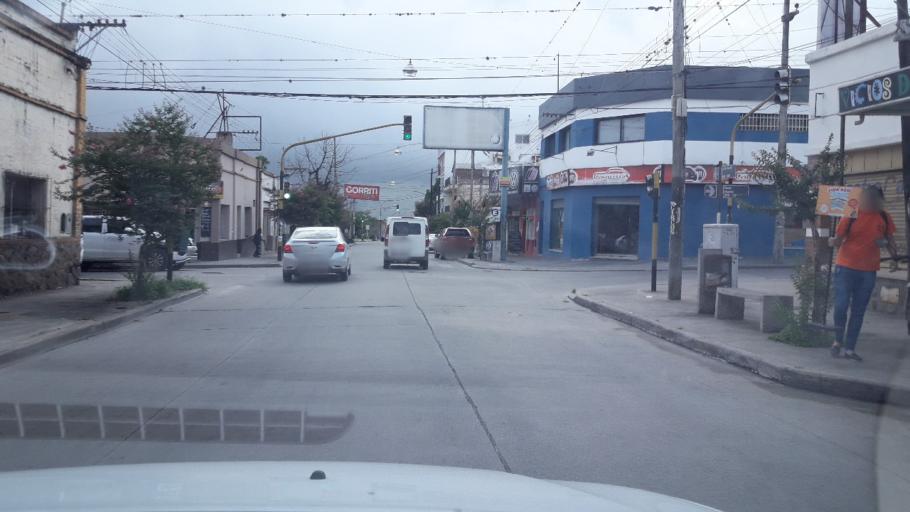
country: AR
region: Jujuy
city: San Salvador de Jujuy
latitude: -24.1918
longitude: -65.2957
